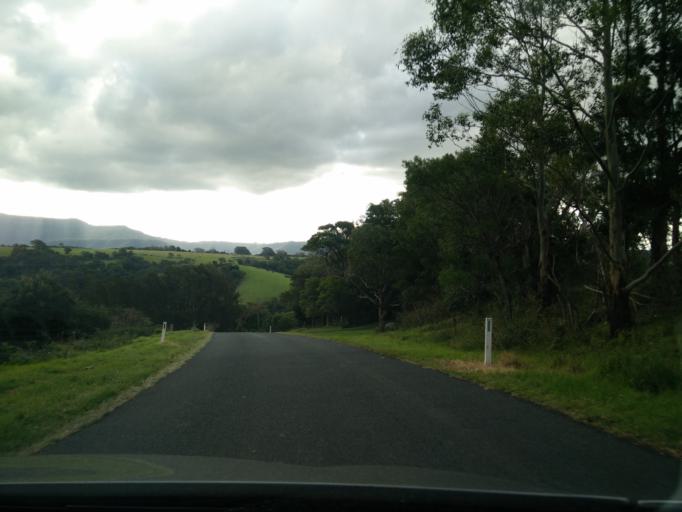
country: AU
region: New South Wales
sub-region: Kiama
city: Jamberoo
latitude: -34.6712
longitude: 150.7927
